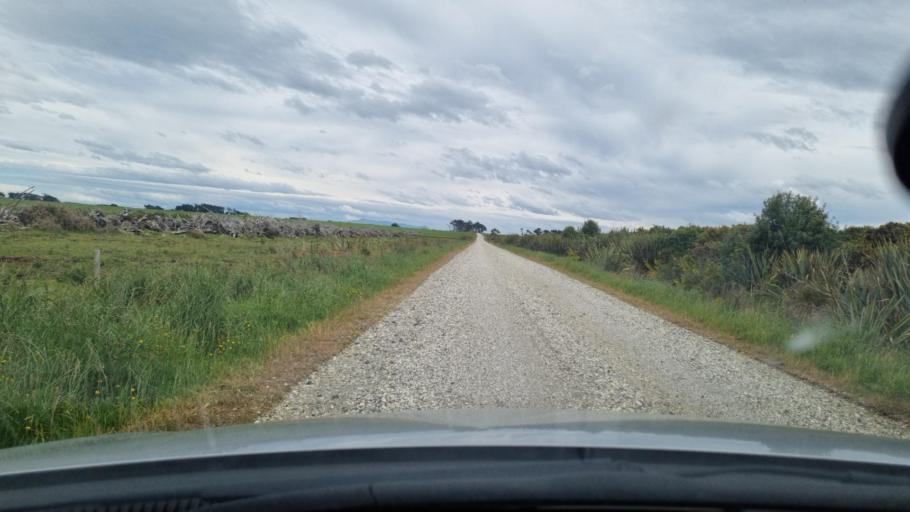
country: NZ
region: Southland
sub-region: Invercargill City
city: Invercargill
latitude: -46.3948
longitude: 168.2696
